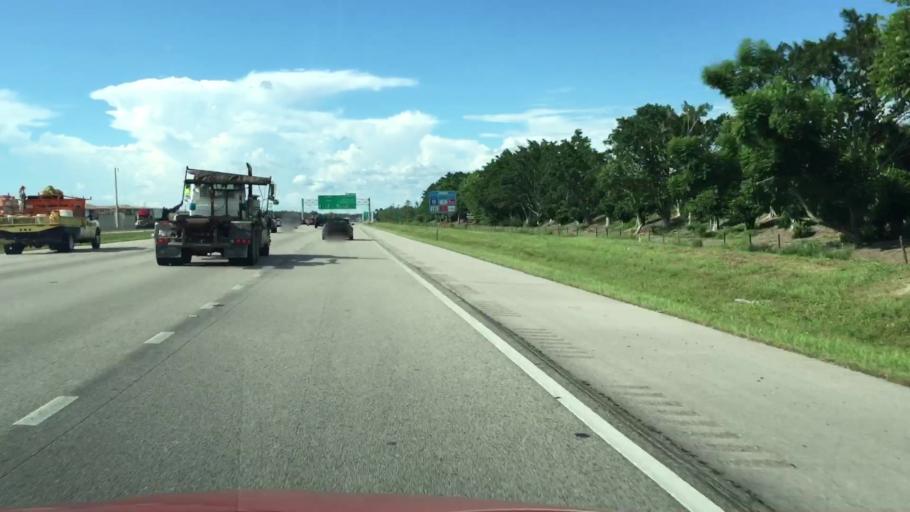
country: US
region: Florida
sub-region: Lee County
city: Three Oaks
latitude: 26.4762
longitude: -81.7913
